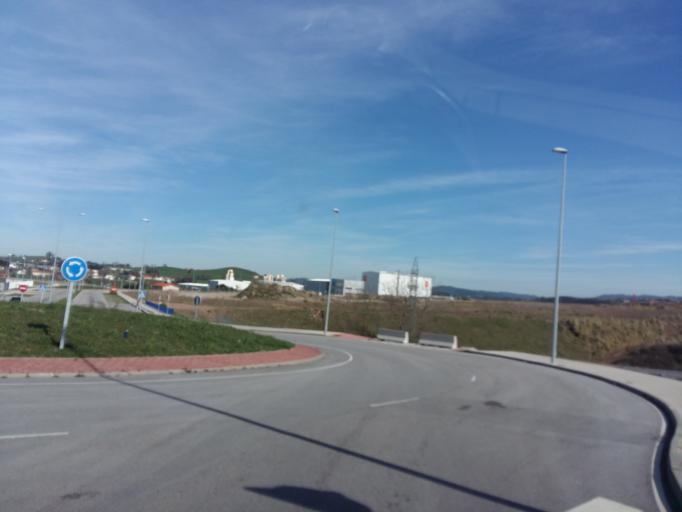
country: ES
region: Cantabria
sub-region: Provincia de Cantabria
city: Lierganes
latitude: 43.3959
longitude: -3.7453
